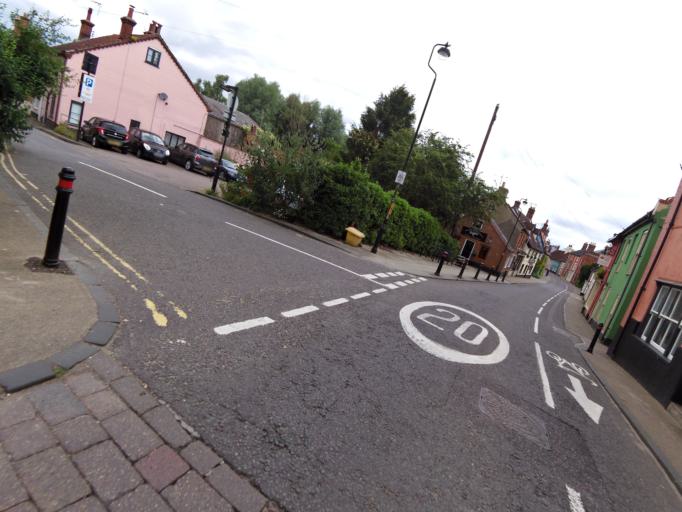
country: GB
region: England
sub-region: Suffolk
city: Bungay
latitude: 52.4566
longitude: 1.4378
